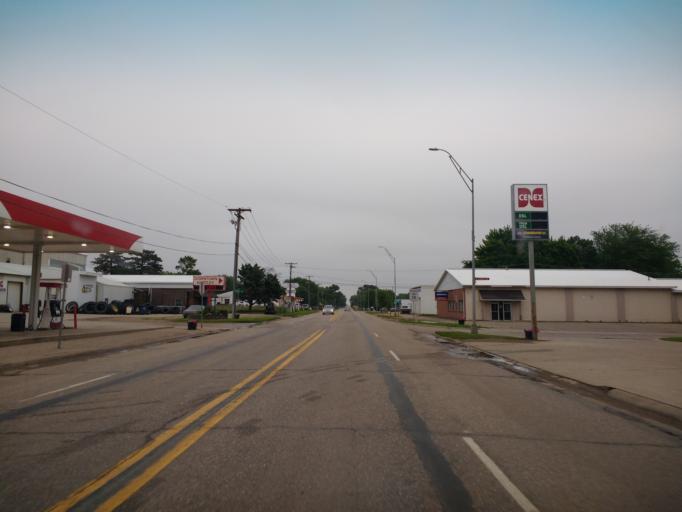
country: US
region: Iowa
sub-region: O'Brien County
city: Hartley
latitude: 43.1848
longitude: -95.4775
